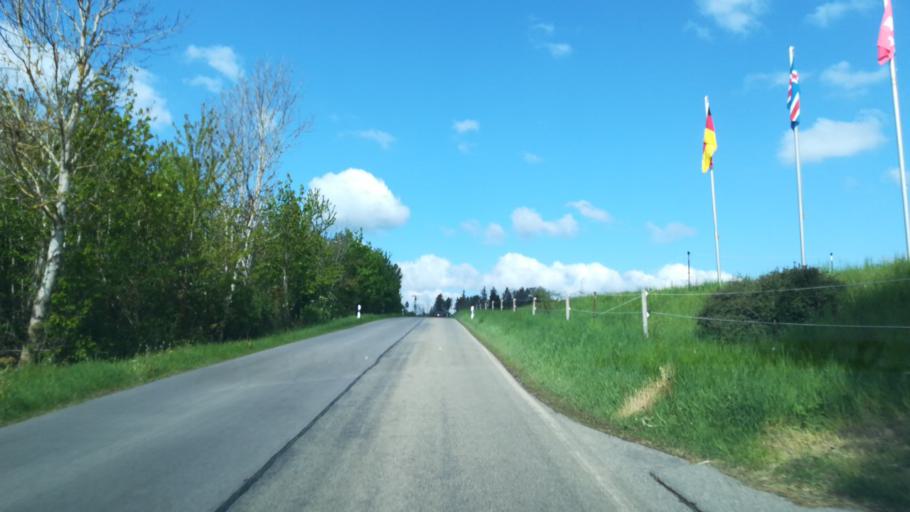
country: DE
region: Baden-Wuerttemberg
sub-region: Freiburg Region
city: Stuhlingen
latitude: 47.7562
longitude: 8.3994
